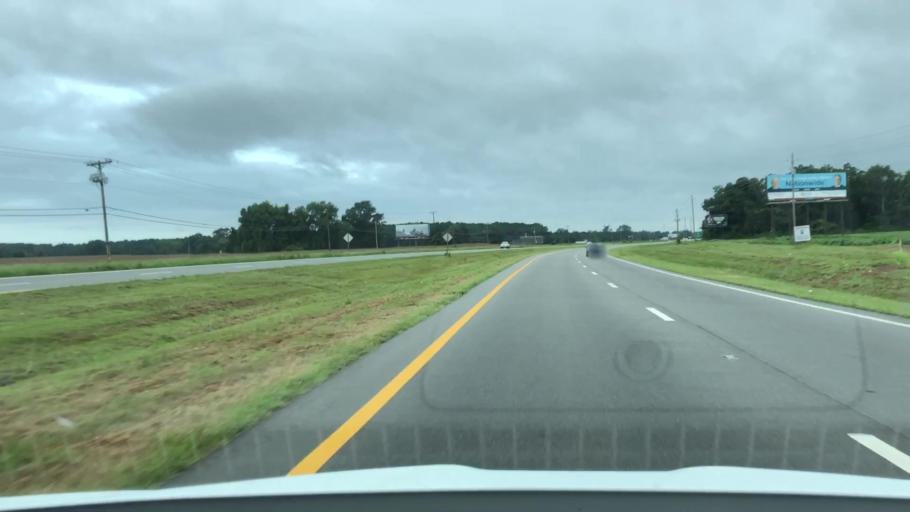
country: US
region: North Carolina
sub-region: Lenoir County
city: Kinston
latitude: 35.2608
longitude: -77.6523
